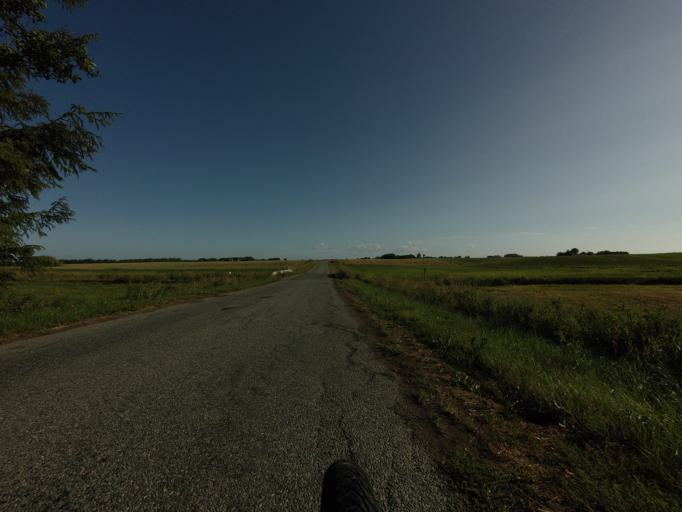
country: DK
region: North Denmark
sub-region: Hjorring Kommune
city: Vra
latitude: 57.3884
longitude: 9.9262
